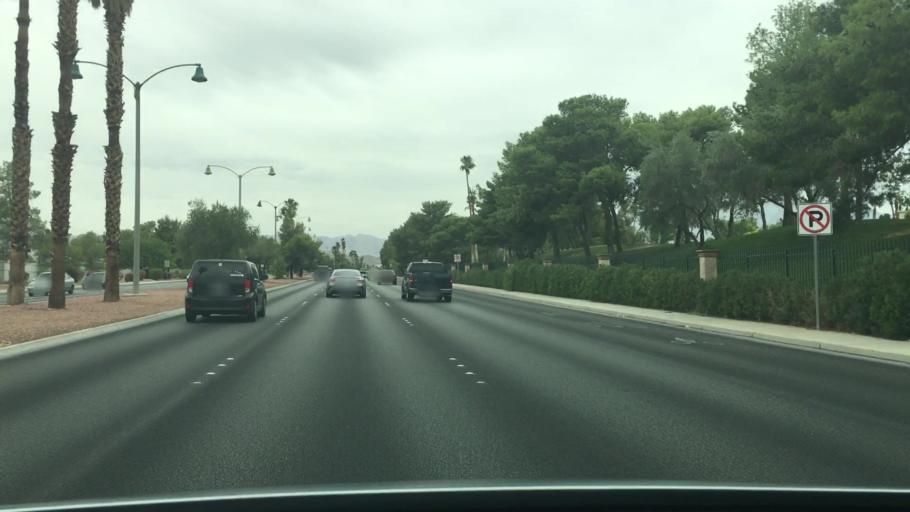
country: US
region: Nevada
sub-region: Clark County
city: Summerlin South
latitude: 36.1441
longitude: -115.2850
